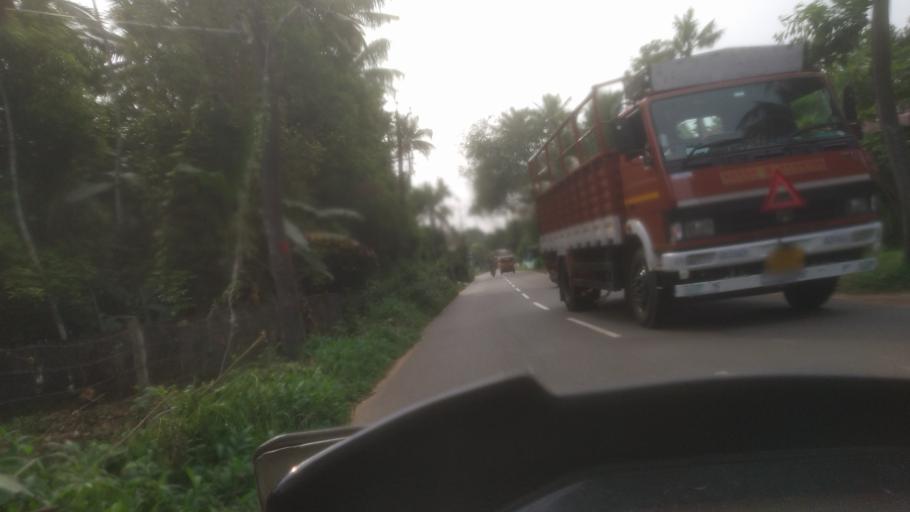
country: IN
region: Kerala
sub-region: Ernakulam
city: Aluva
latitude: 10.1560
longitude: 76.3225
